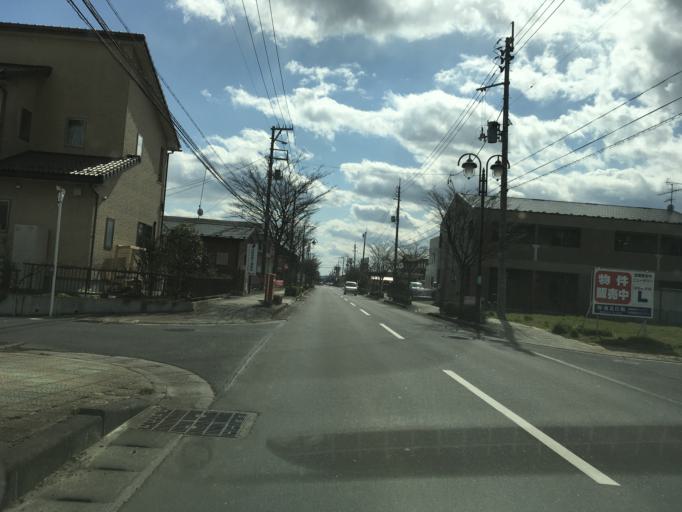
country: JP
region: Miyagi
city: Wakuya
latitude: 38.7045
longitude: 141.2141
